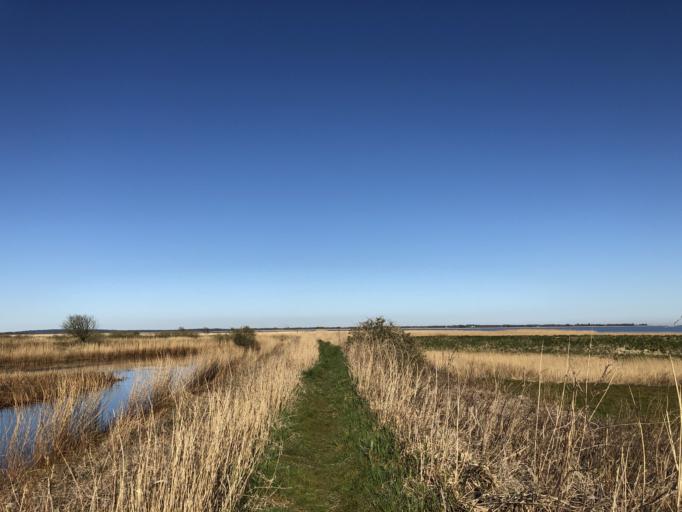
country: DK
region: Central Jutland
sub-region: Holstebro Kommune
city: Ulfborg
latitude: 56.2962
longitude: 8.2777
